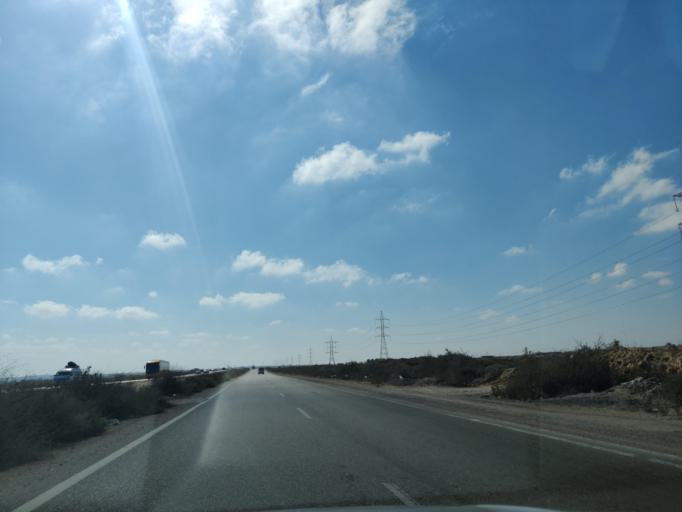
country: EG
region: Muhafazat Matruh
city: Al `Alamayn
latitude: 31.0499
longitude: 28.3293
